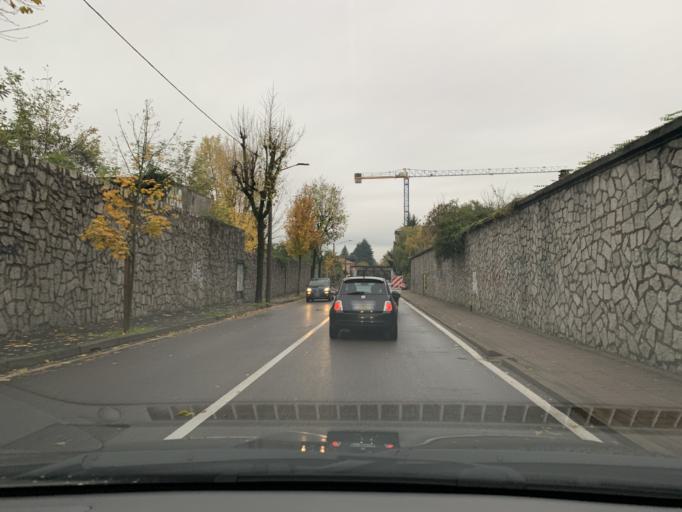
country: IT
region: Lombardy
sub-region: Provincia di Varese
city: Saronno
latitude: 45.6299
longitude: 9.0464
